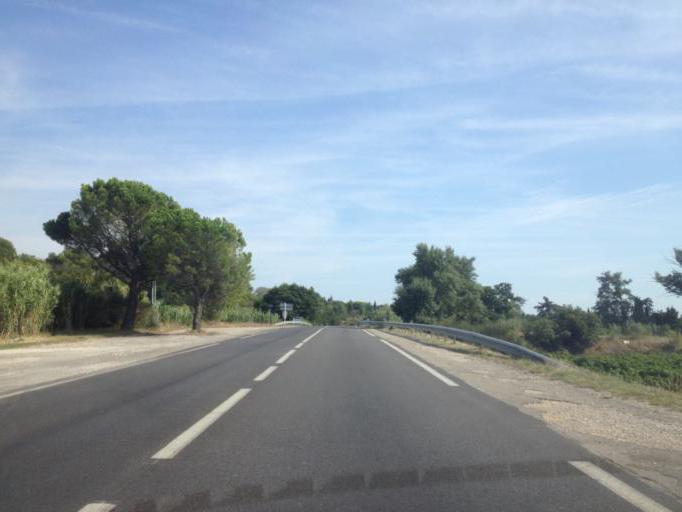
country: FR
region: Provence-Alpes-Cote d'Azur
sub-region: Departement du Vaucluse
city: Beaumes-de-Venise
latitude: 44.1151
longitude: 5.0177
